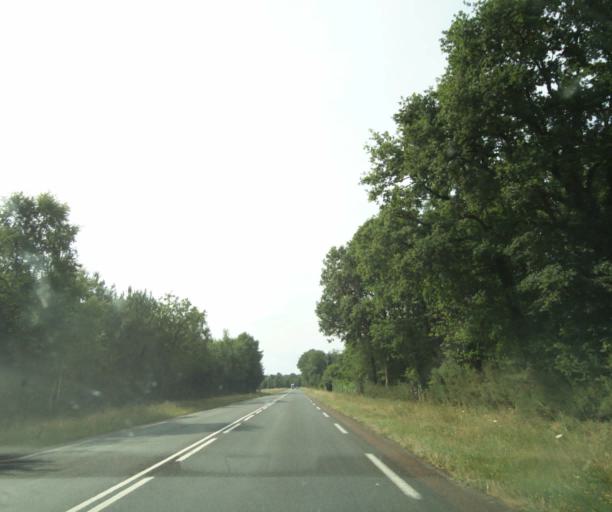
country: FR
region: Pays de la Loire
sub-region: Departement de la Sarthe
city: Marigne-Laille
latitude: 47.8002
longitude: 0.3276
